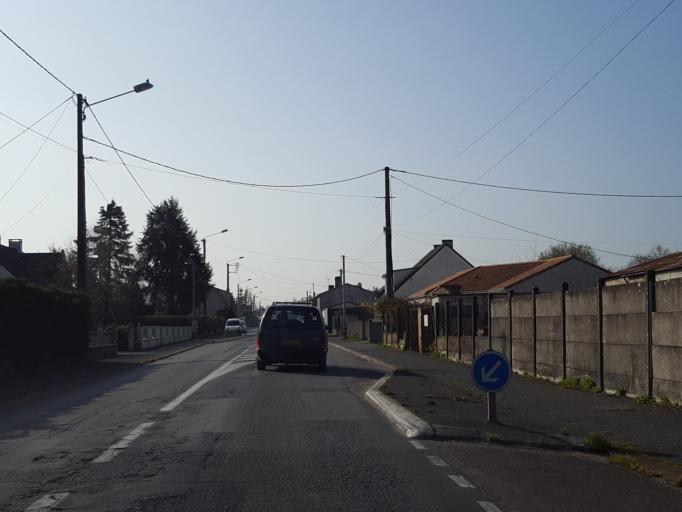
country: FR
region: Pays de la Loire
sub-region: Departement de la Loire-Atlantique
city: Geneston
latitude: 47.0610
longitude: -1.5155
